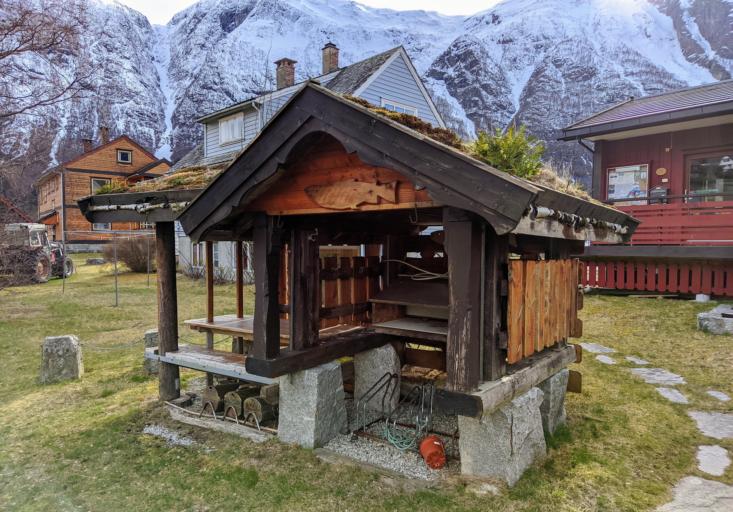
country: NO
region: Hordaland
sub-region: Eidfjord
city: Eidfjord
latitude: 60.4693
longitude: 7.0716
